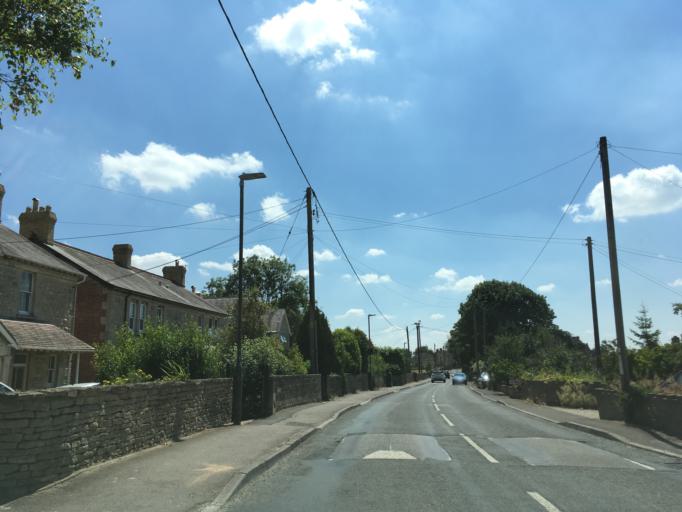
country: GB
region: England
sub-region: Gloucestershire
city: Stroud
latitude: 51.7590
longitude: -2.2321
